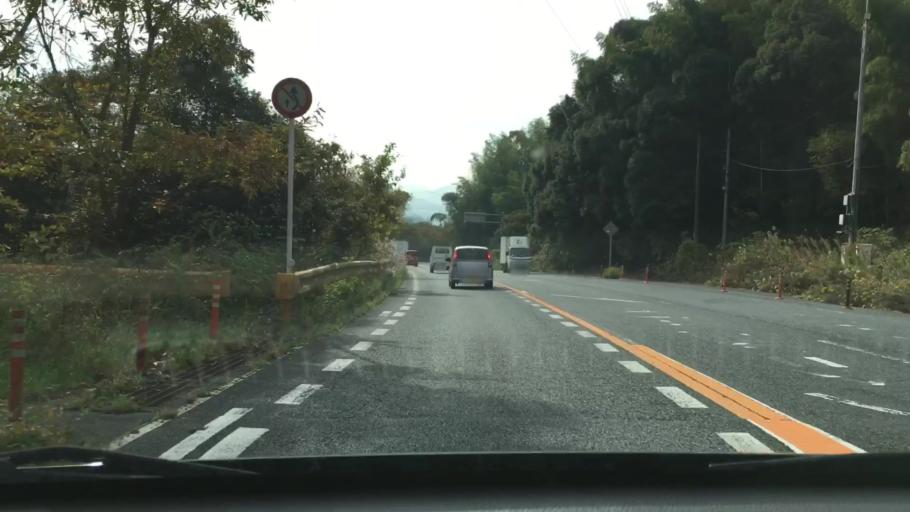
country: JP
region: Yamaguchi
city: Iwakuni
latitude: 34.1101
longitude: 132.1086
